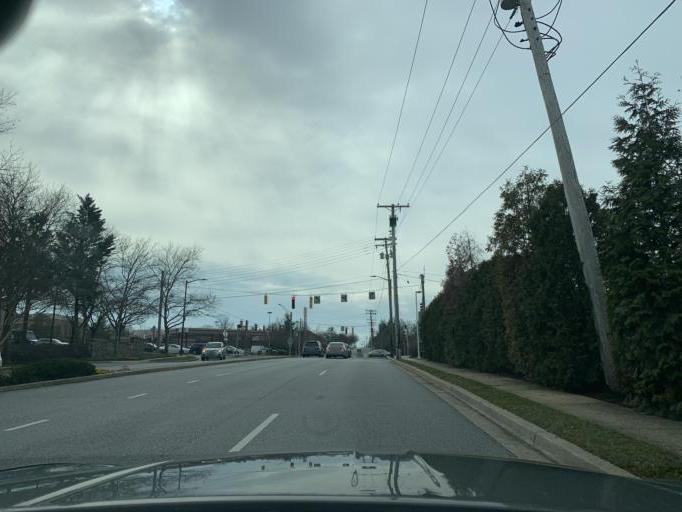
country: US
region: Maryland
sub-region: Anne Arundel County
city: Maryland City
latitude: 39.0998
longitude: -76.8103
